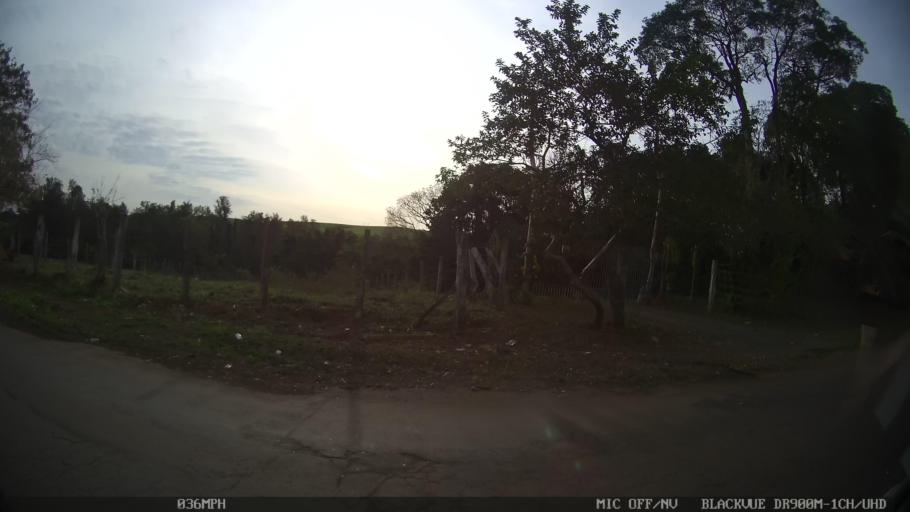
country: BR
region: Sao Paulo
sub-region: Piracicaba
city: Piracicaba
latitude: -22.6944
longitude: -47.5841
